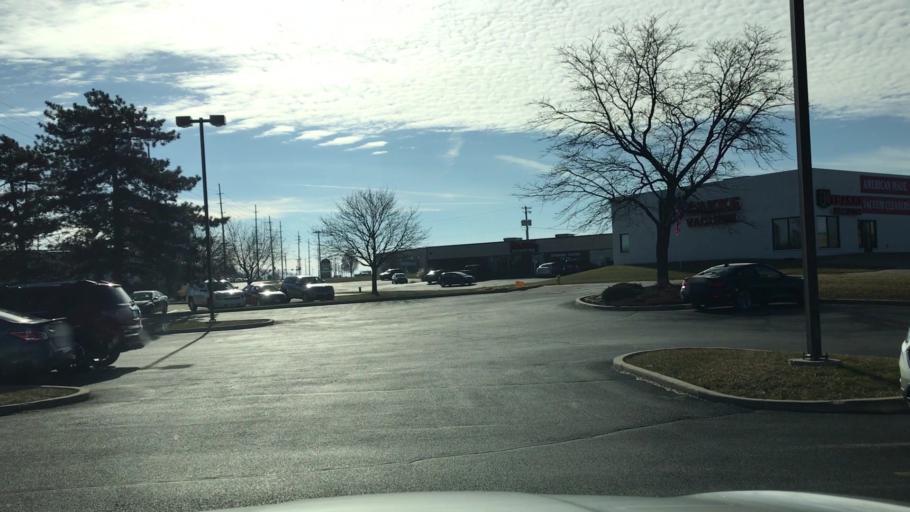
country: US
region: Illinois
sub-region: McLean County
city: Normal
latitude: 40.5009
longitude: -88.9538
